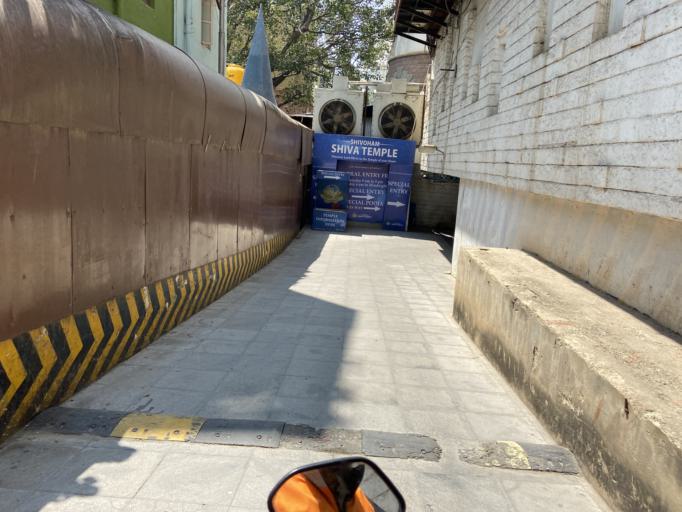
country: IN
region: Karnataka
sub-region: Bangalore Urban
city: Bangalore
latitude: 12.9590
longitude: 77.6571
